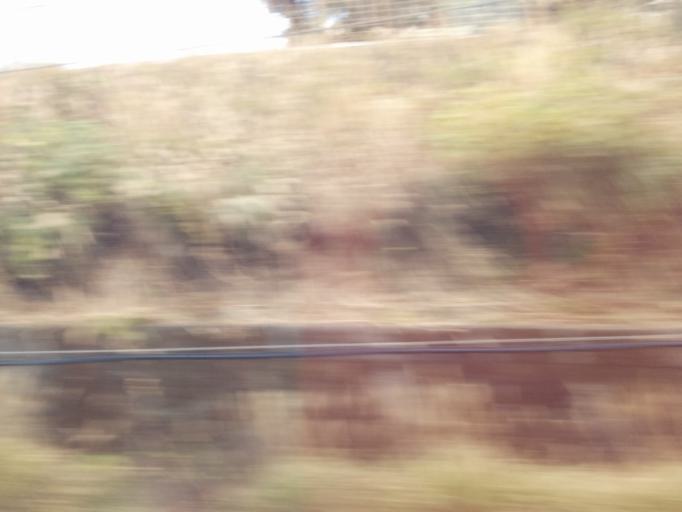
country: JP
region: Shizuoka
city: Fuji
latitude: 35.1524
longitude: 138.7734
